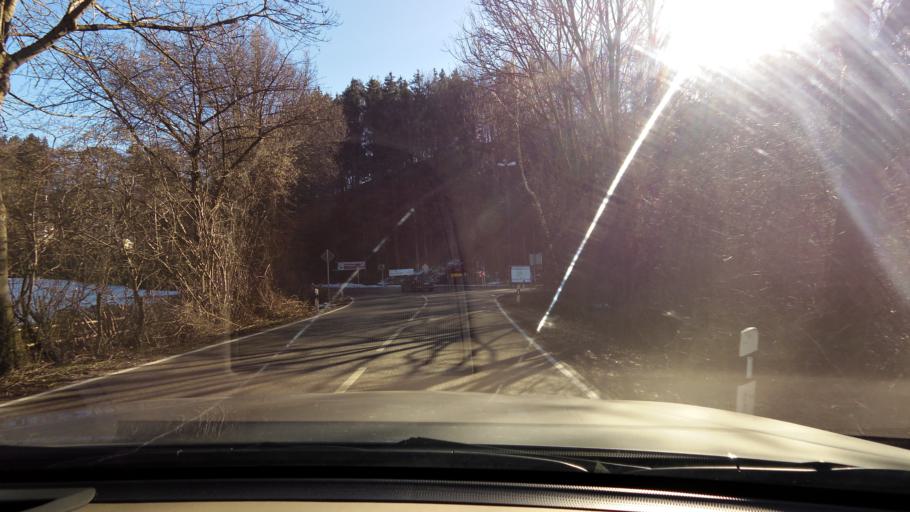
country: DE
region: Bavaria
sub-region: Upper Bavaria
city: Kraiburg am Inn
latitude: 48.1863
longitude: 12.4457
